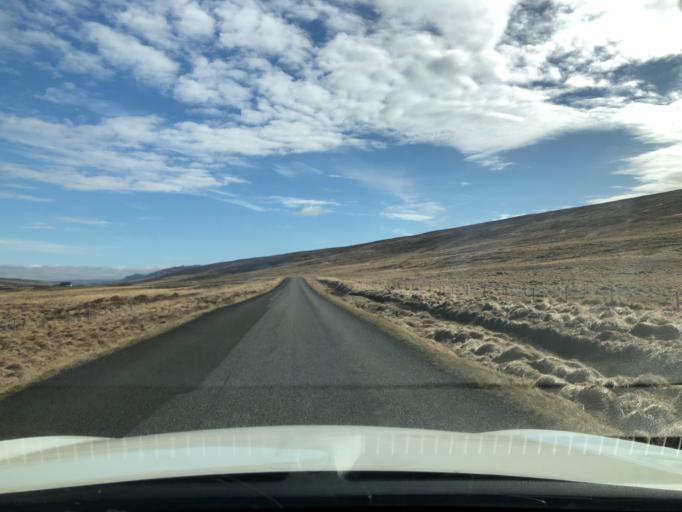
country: IS
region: West
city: Borgarnes
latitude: 65.0905
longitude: -21.7380
